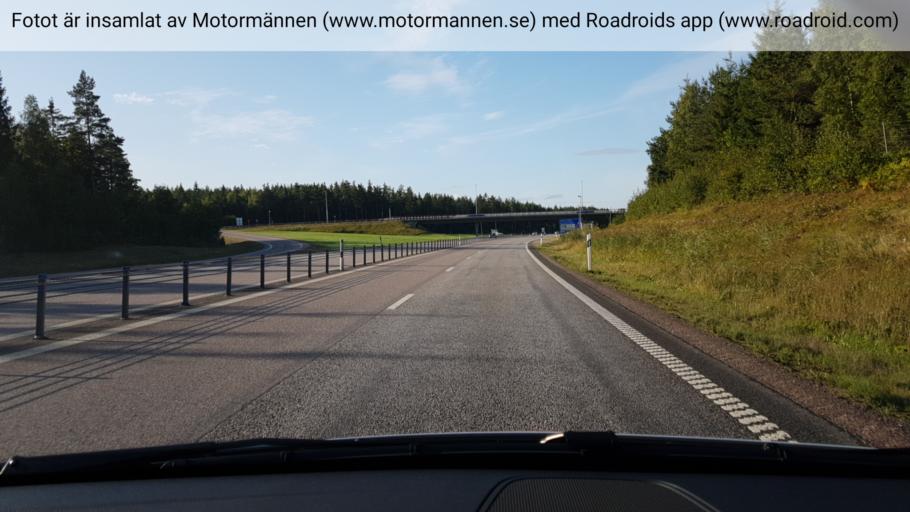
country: SE
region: Vaestra Goetaland
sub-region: Skovde Kommun
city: Skultorp
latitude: 58.3426
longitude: 13.8650
